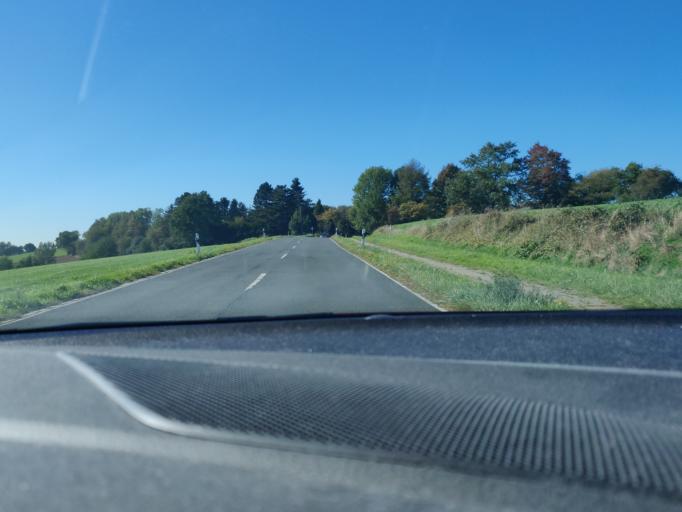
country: DE
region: North Rhine-Westphalia
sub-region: Regierungsbezirk Dusseldorf
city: Heiligenhaus
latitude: 51.3430
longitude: 6.9641
